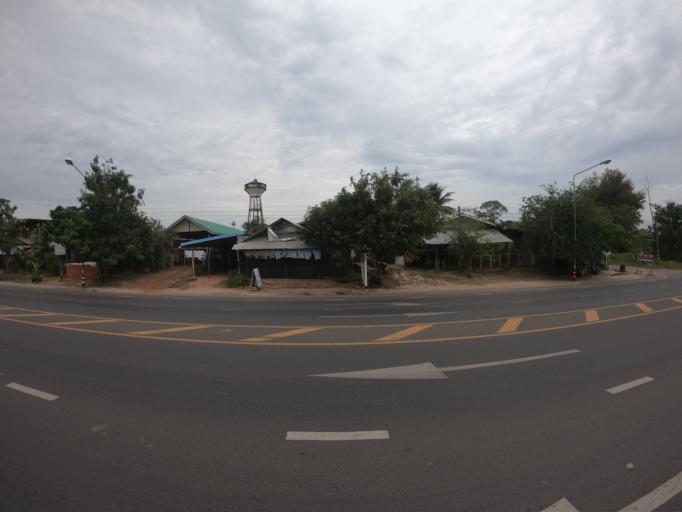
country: TH
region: Roi Et
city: Chiang Khwan
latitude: 16.1478
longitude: 103.8593
